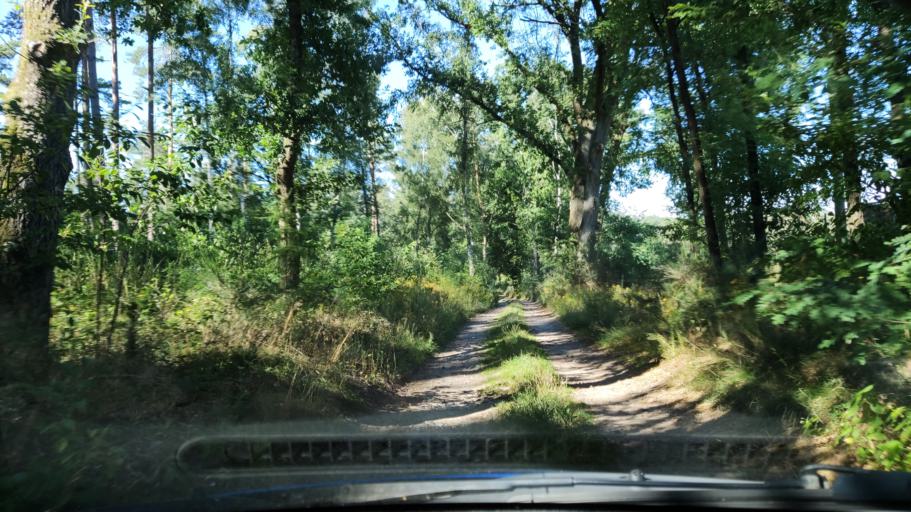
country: DE
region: Lower Saxony
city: Thomasburg
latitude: 53.1797
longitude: 10.6714
